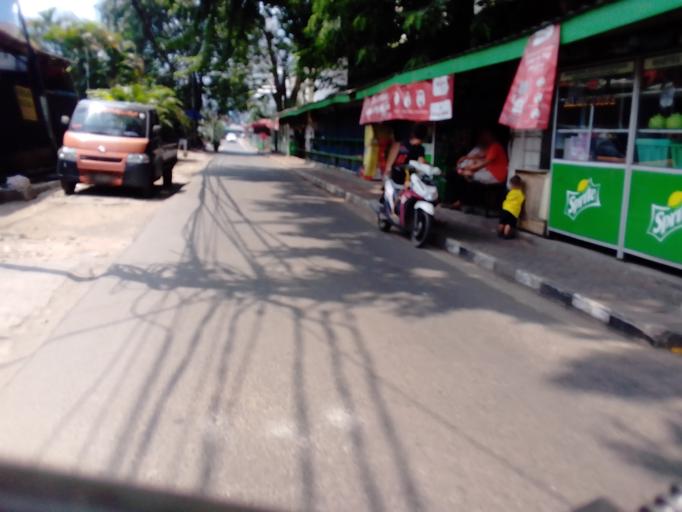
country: ID
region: Jakarta Raya
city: Jakarta
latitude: -6.2167
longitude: 106.8131
